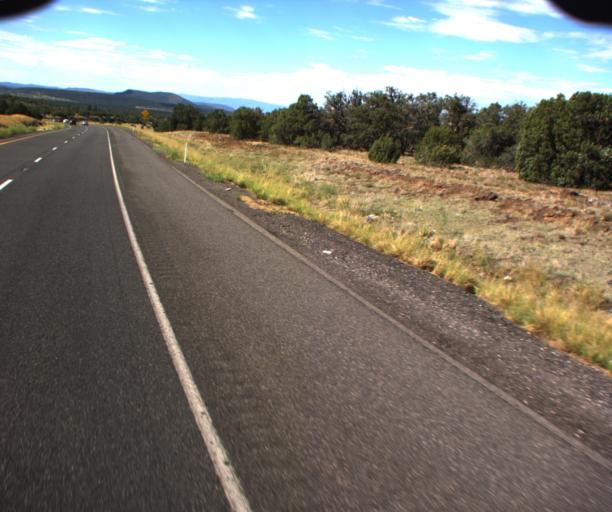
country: US
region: Arizona
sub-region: Yavapai County
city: Village of Oak Creek (Big Park)
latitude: 34.8028
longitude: -111.5981
